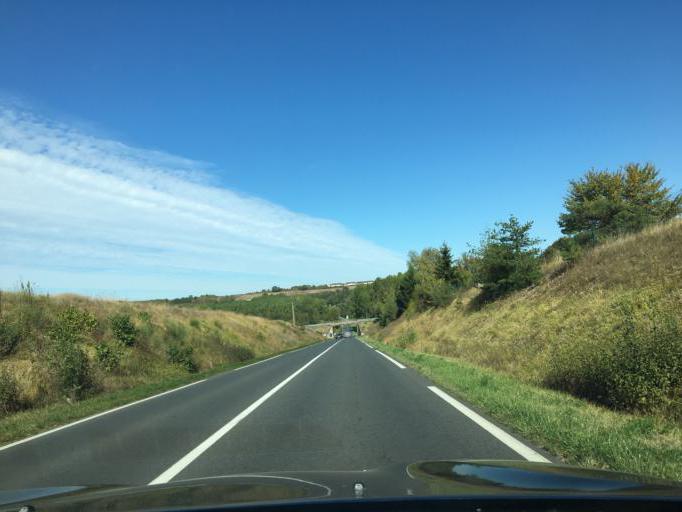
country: FR
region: Centre
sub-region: Departement d'Indre-et-Loire
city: Azay-le-Rideau
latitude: 47.2539
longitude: 0.4547
